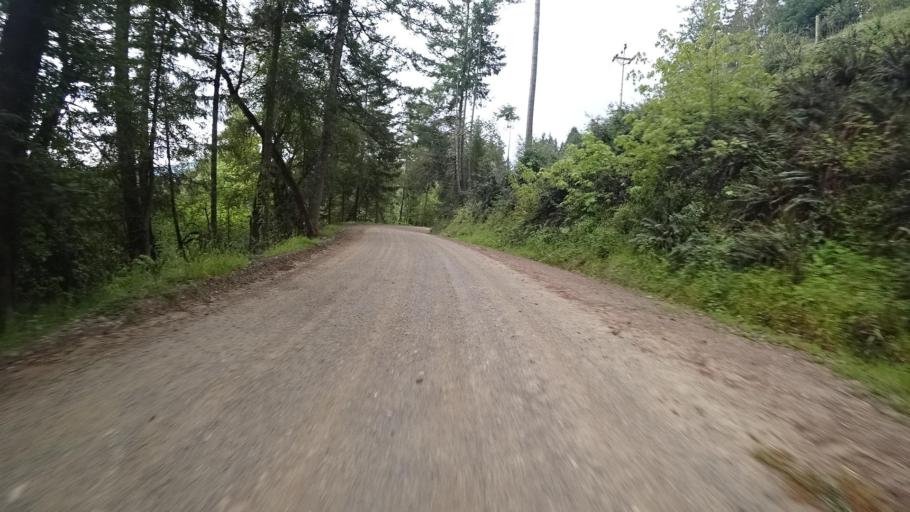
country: US
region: California
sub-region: Humboldt County
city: Redway
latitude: 40.2508
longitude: -123.7654
